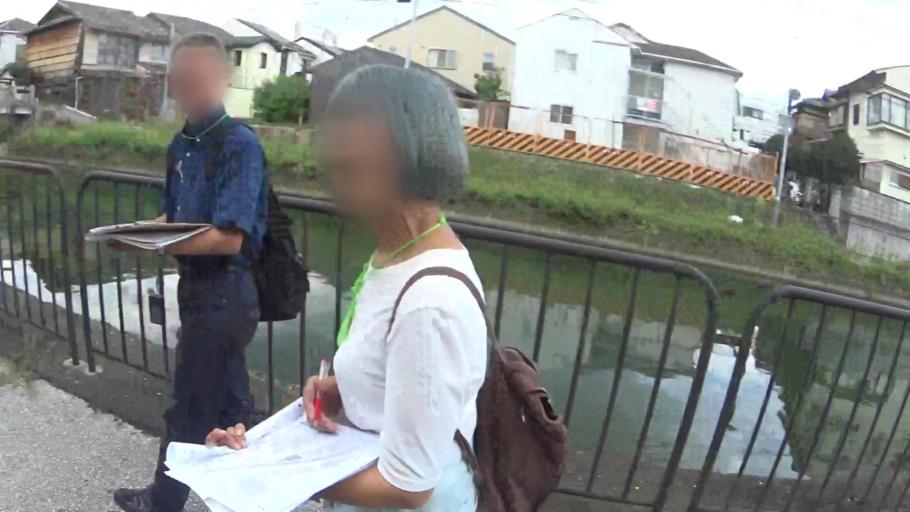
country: JP
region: Kyoto
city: Muko
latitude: 34.9492
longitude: 135.7687
